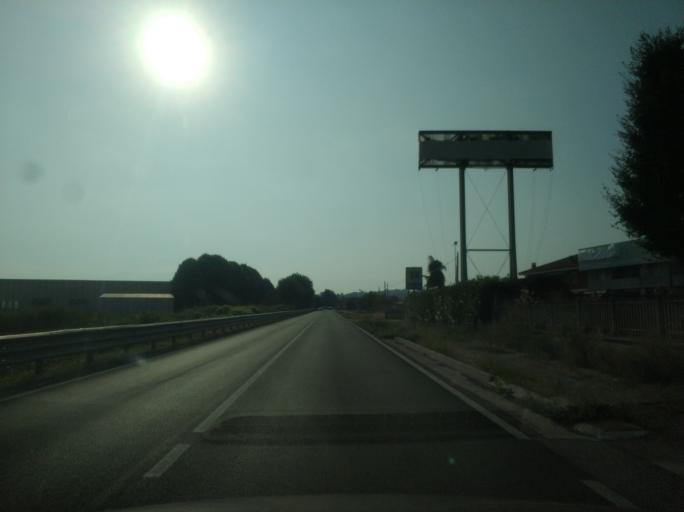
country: IT
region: Piedmont
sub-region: Provincia di Cuneo
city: Cinzano
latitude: 44.6950
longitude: 7.9056
